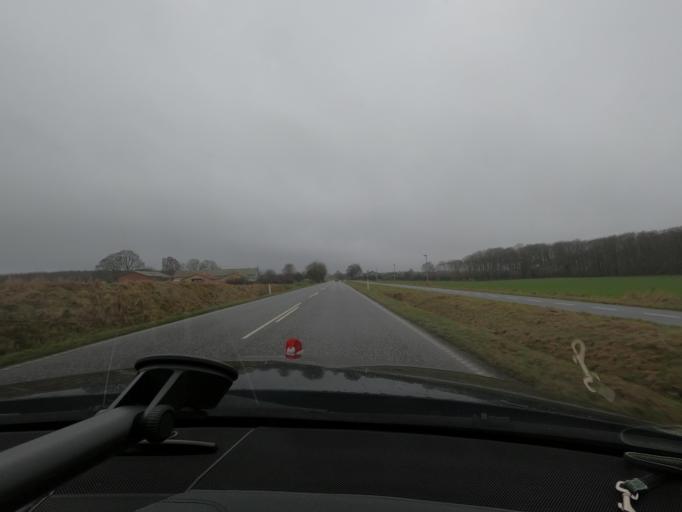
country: DK
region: South Denmark
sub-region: Sonderborg Kommune
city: Horuphav
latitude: 54.9052
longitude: 9.8654
